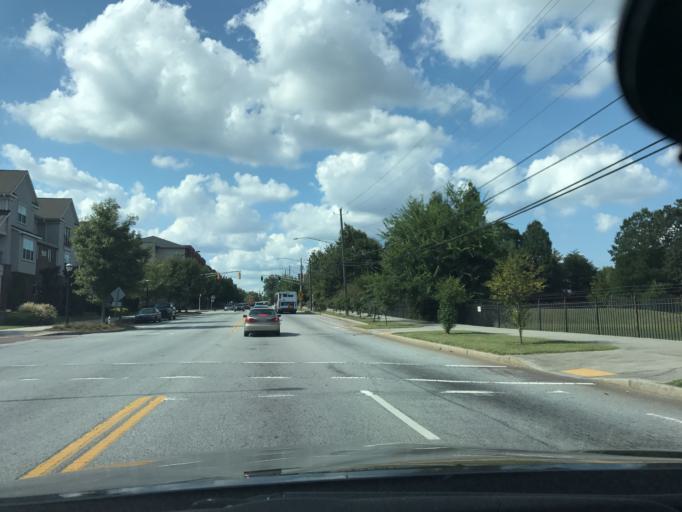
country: US
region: Georgia
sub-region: Fulton County
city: Atlanta
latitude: 33.7392
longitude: -84.4020
